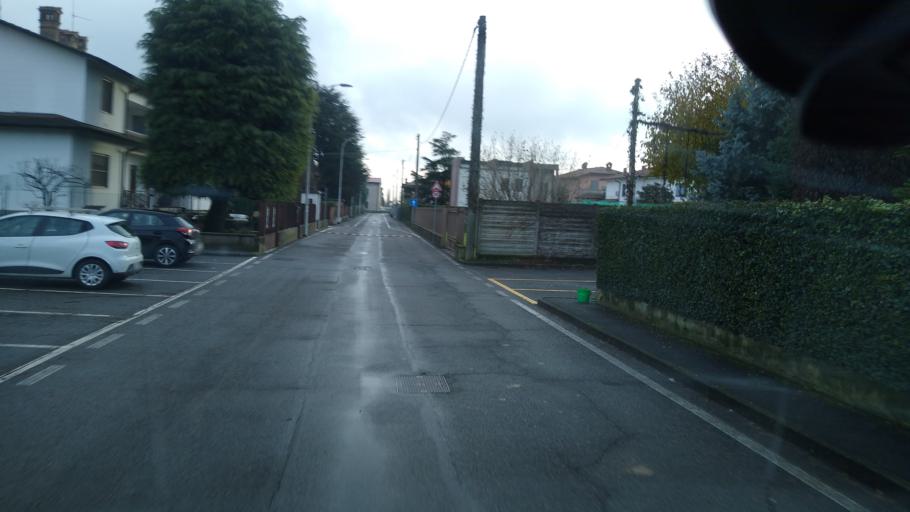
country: IT
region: Lombardy
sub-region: Provincia di Bergamo
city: Misano di Gera d'Adda
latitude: 45.4702
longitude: 9.6234
